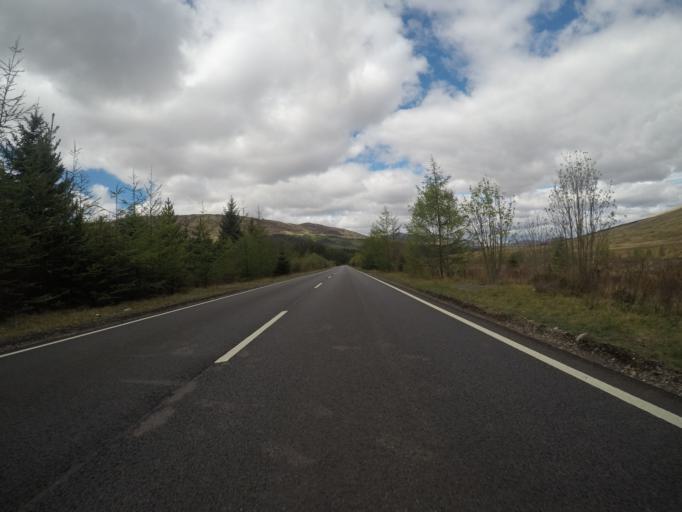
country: GB
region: Scotland
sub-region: Highland
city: Spean Bridge
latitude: 56.5003
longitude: -4.7623
